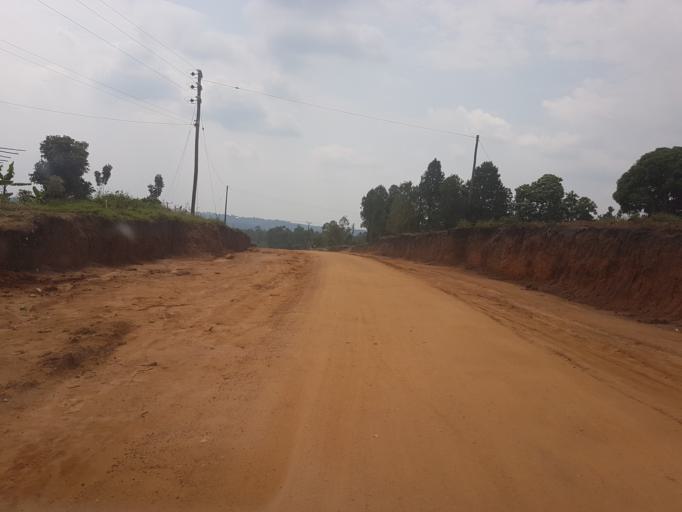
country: UG
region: Western Region
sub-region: Kanungu District
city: Ntungamo
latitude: -0.8150
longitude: 29.7065
